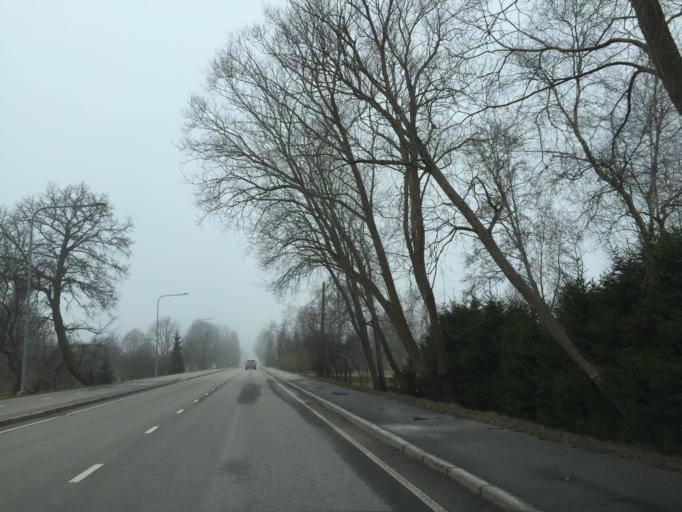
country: EE
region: Saare
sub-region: Kuressaare linn
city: Kuressaare
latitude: 58.2291
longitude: 22.3963
